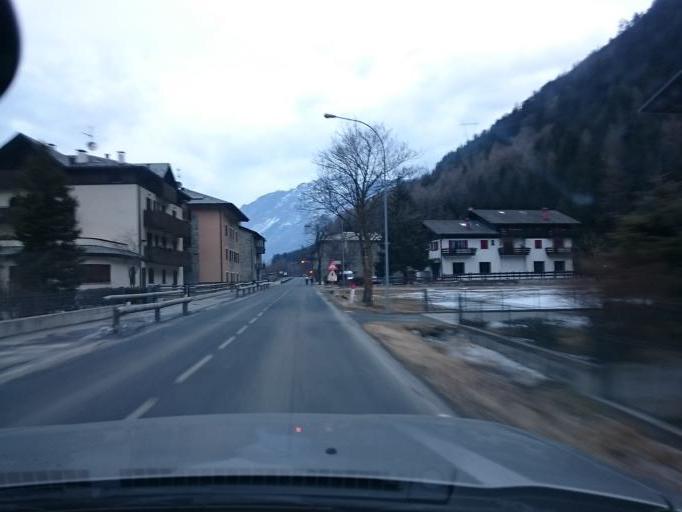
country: IT
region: Lombardy
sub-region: Provincia di Sondrio
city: Valdisotto
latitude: 46.4224
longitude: 10.3547
